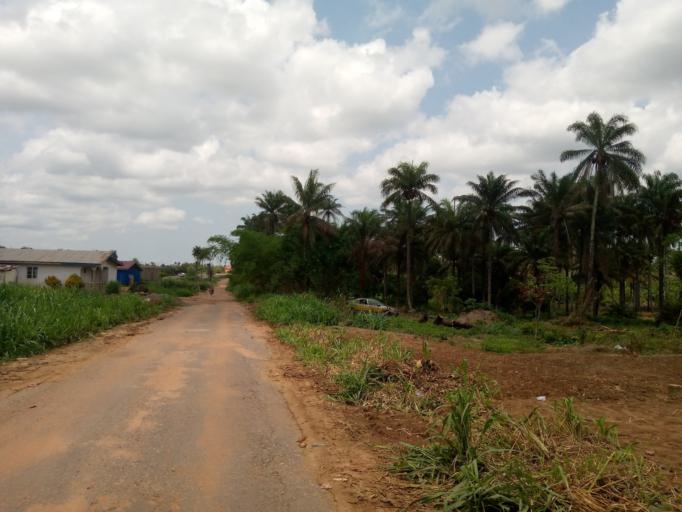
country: SL
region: Western Area
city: Waterloo
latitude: 8.3763
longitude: -12.9595
